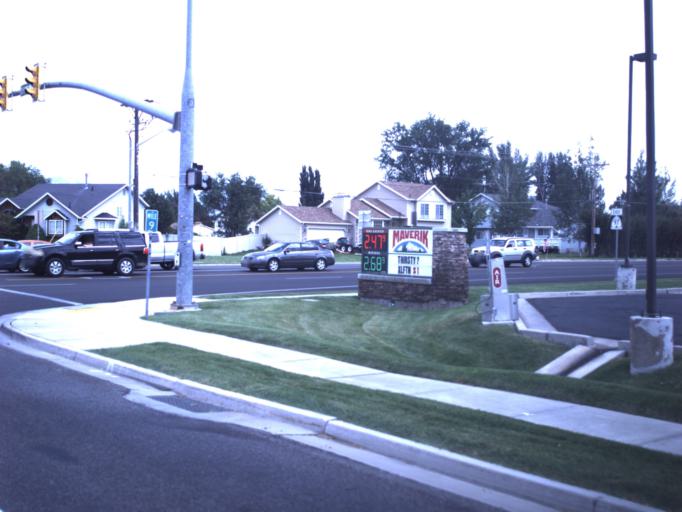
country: US
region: Utah
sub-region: Davis County
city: Clinton
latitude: 41.1613
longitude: -112.0644
